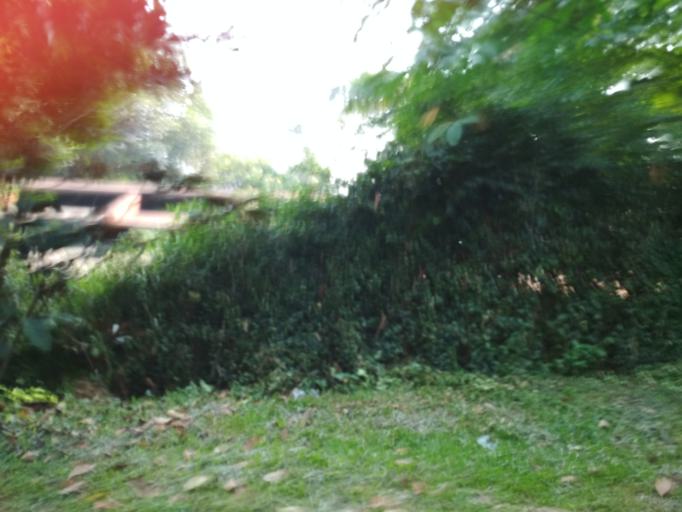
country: ID
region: West Java
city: Ciampea
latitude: -6.5558
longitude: 106.7286
